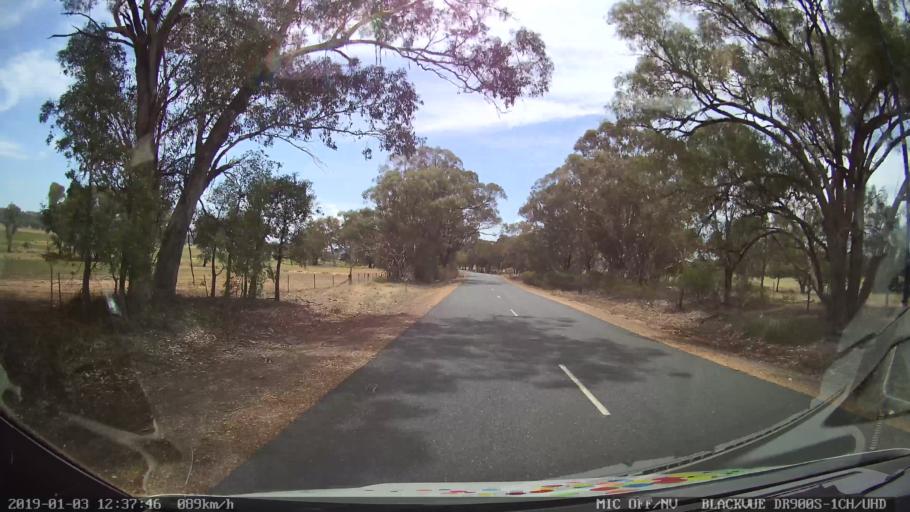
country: AU
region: New South Wales
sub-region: Weddin
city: Grenfell
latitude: -33.8397
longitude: 148.1879
